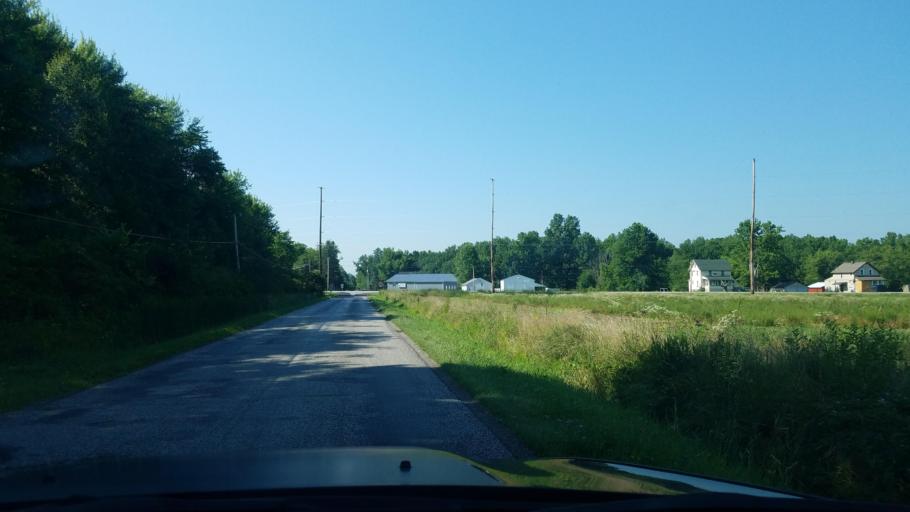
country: US
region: Ohio
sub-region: Trumbull County
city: Leavittsburg
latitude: 41.2789
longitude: -80.9059
